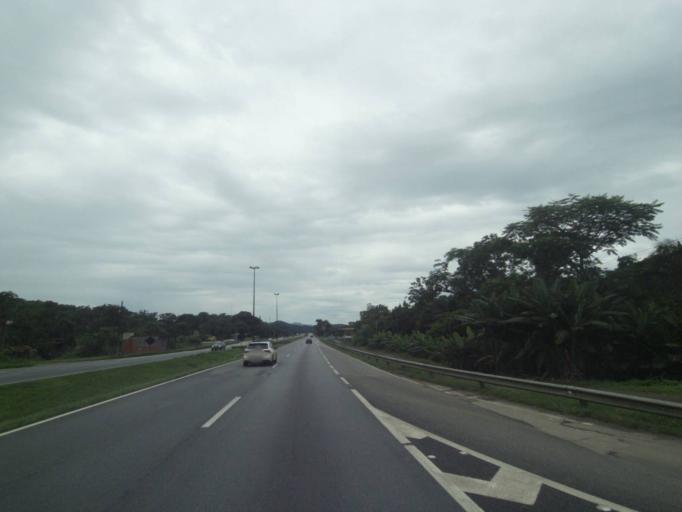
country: BR
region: Parana
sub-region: Antonina
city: Antonina
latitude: -25.5528
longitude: -48.7999
